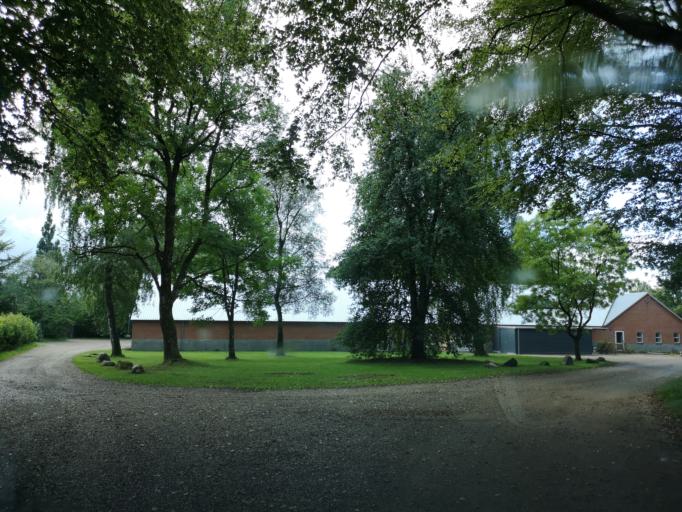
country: DK
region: Central Jutland
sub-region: Holstebro Kommune
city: Holstebro
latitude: 56.3346
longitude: 8.6376
